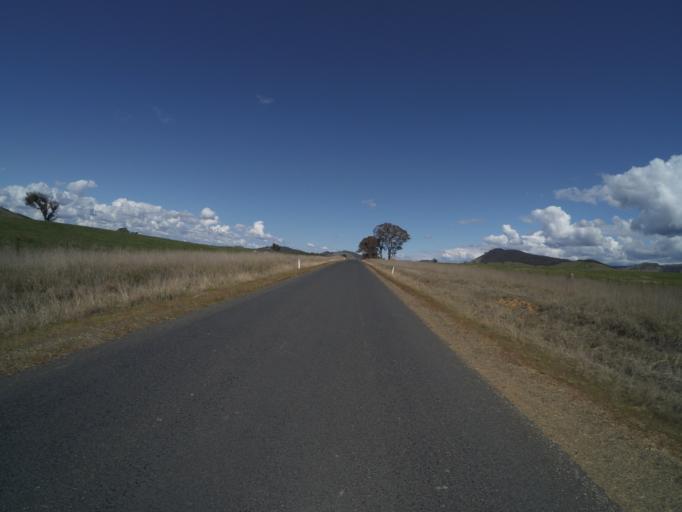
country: AU
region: New South Wales
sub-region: Yass Valley
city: Murrumbateman
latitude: -35.1218
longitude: 148.8671
